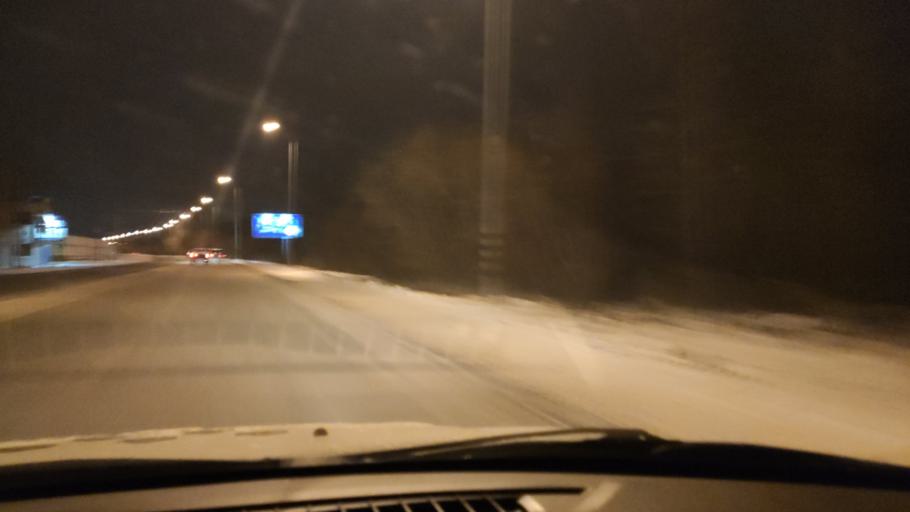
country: RU
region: Perm
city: Perm
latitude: 58.1049
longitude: 56.3227
